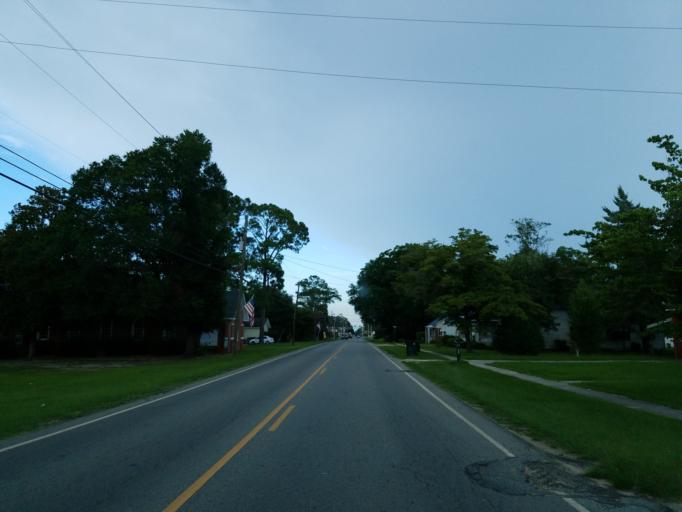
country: US
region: Georgia
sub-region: Cook County
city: Sparks
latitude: 31.2712
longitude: -83.4681
